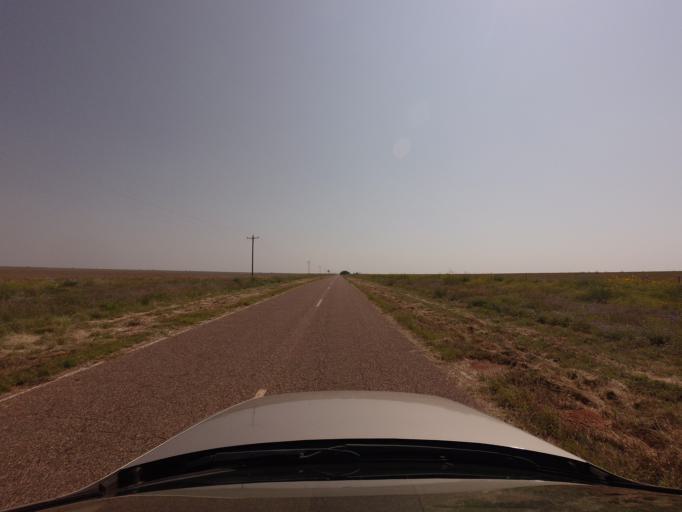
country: US
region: New Mexico
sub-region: Curry County
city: Cannon Air Force Base
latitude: 34.6336
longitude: -103.6334
